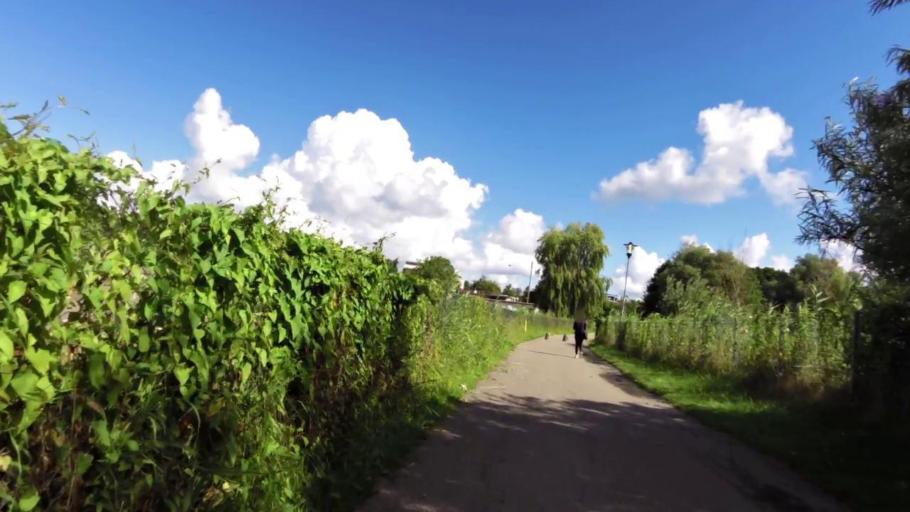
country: PL
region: West Pomeranian Voivodeship
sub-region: Powiat koszalinski
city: Mielno
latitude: 54.2572
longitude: 16.0572
